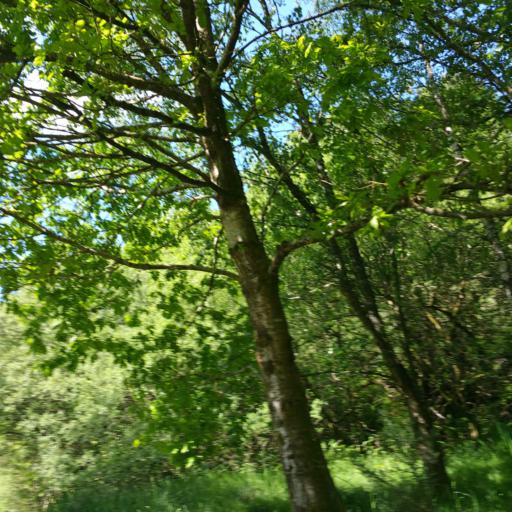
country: GB
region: Scotland
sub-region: East Dunbartonshire
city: Milngavie
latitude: 55.9523
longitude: -4.3209
